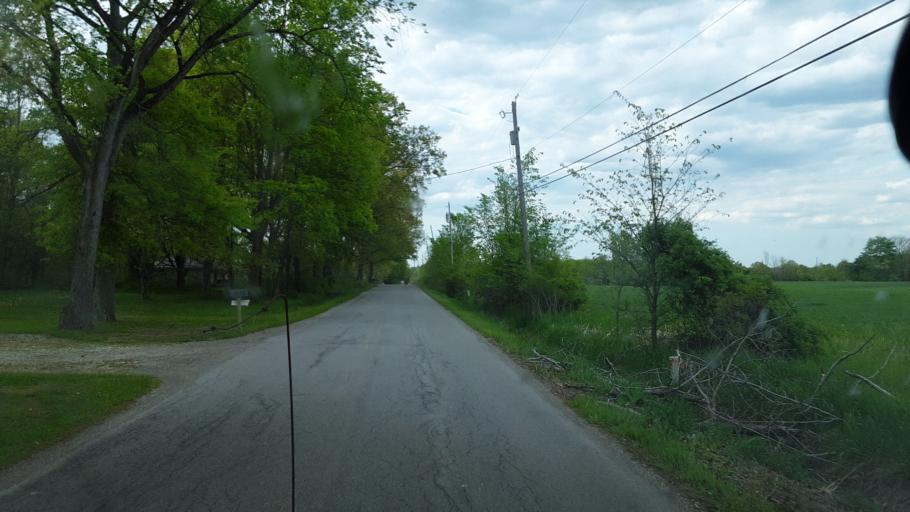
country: US
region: Ohio
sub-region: Portage County
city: Windham
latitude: 41.3027
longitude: -80.9835
